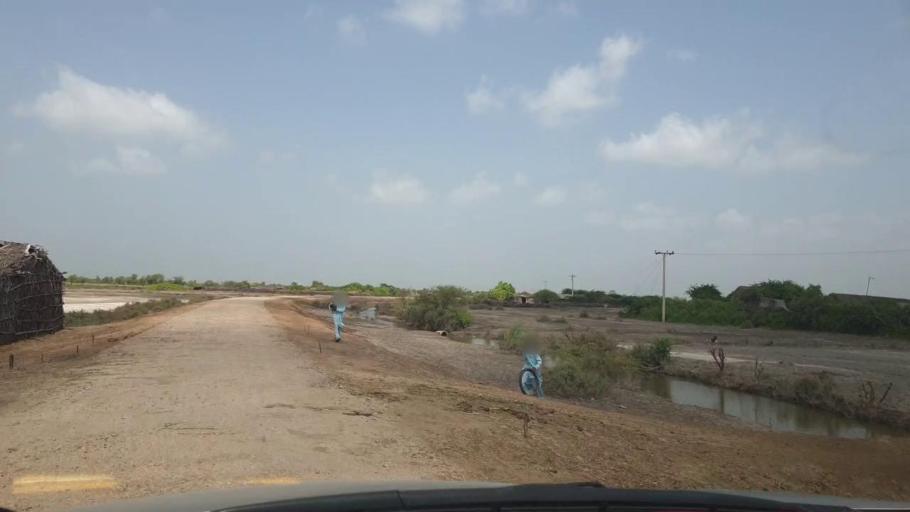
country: PK
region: Sindh
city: Rajo Khanani
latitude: 24.9230
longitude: 68.8979
